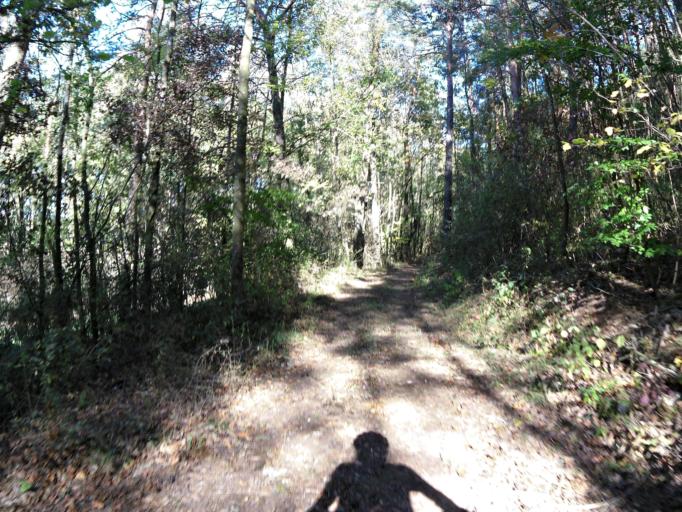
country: DE
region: Bavaria
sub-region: Regierungsbezirk Unterfranken
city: Eibelstadt
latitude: 49.7154
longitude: 9.9832
